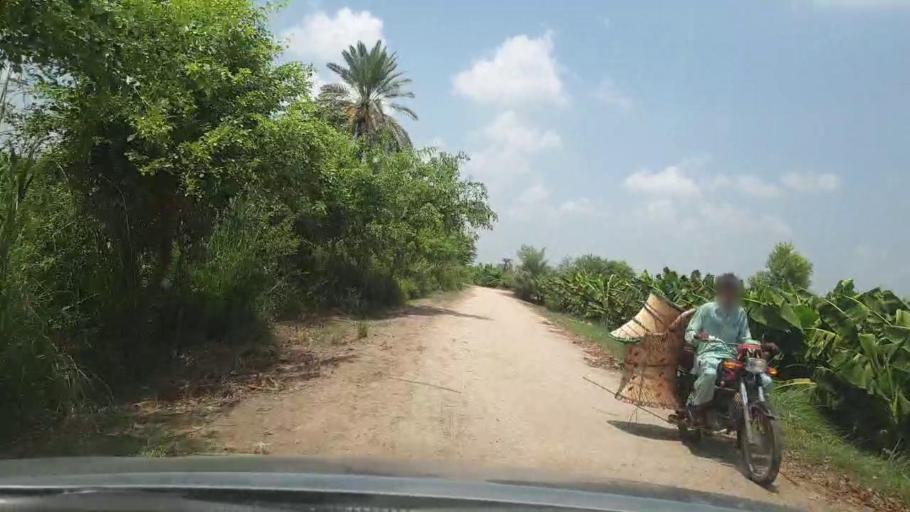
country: PK
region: Sindh
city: Pir jo Goth
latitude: 27.6048
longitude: 68.6121
